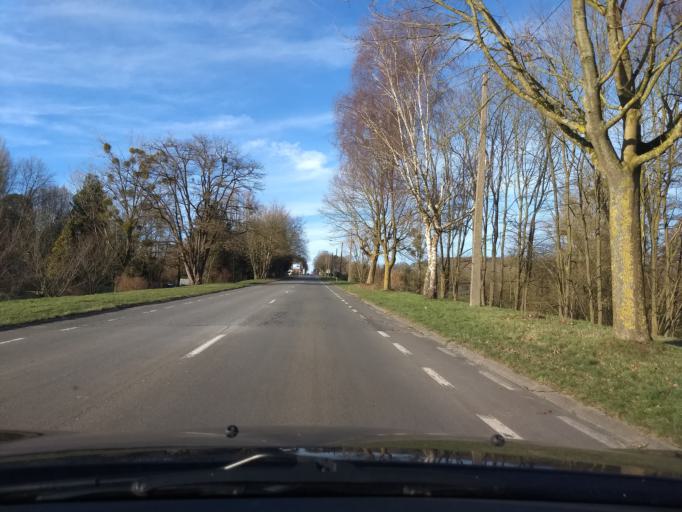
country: BE
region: Wallonia
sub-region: Province du Brabant Wallon
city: Braine-le-Chateau
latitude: 50.6878
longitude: 4.2705
